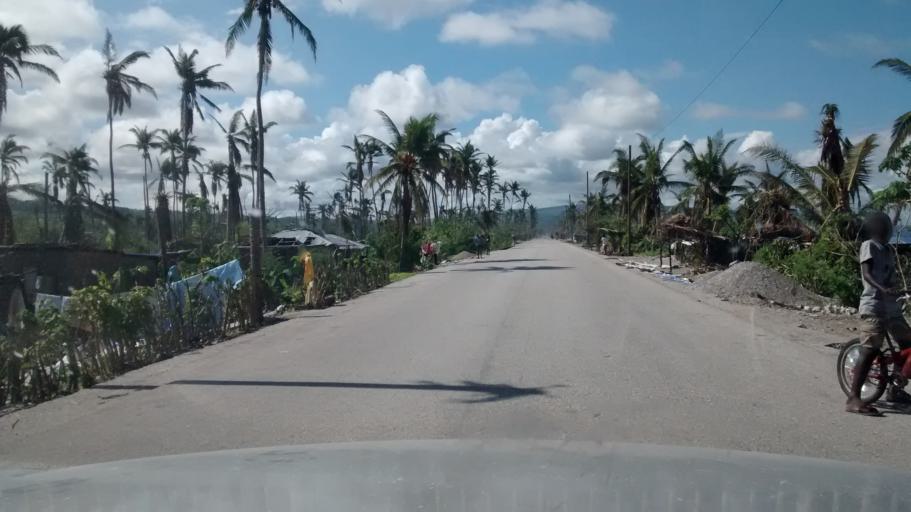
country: HT
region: Grandans
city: Jeremie
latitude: 18.6038
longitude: -74.0393
